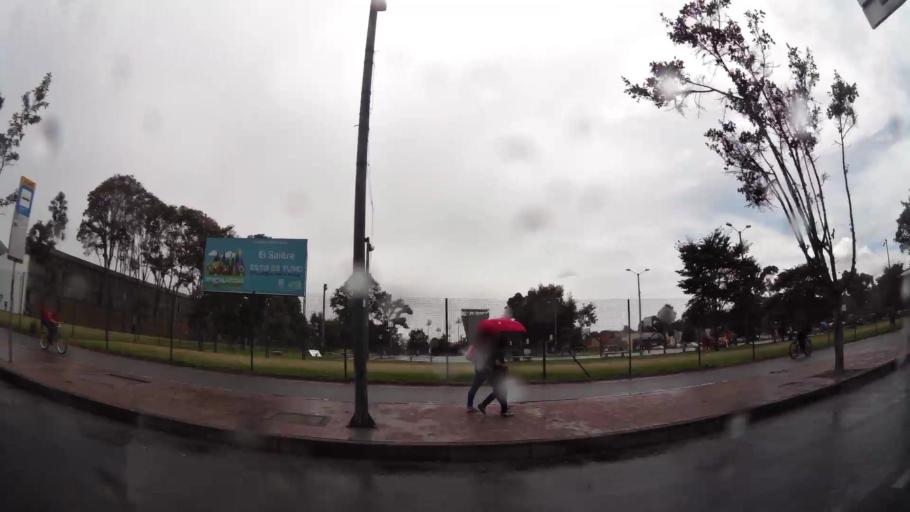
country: CO
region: Bogota D.C.
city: Bogota
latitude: 4.6674
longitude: -74.0957
